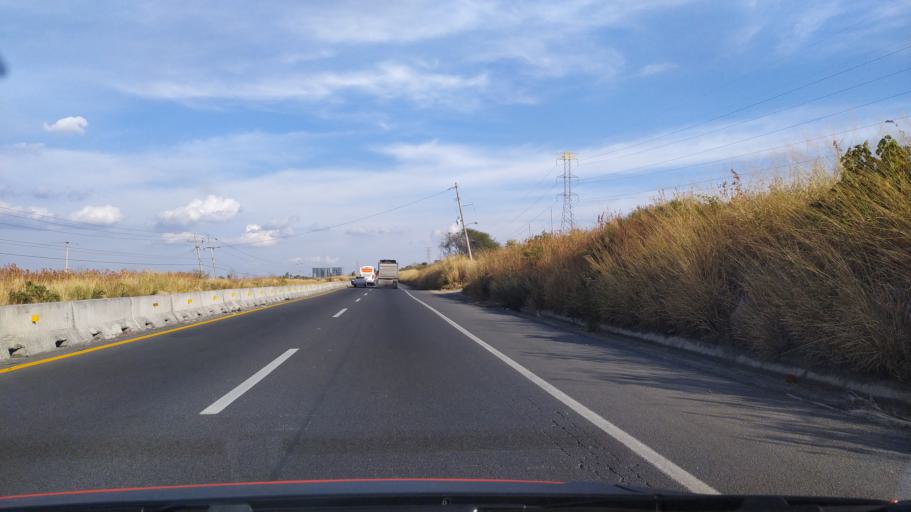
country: MX
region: Jalisco
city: Atotonilquillo
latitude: 20.3956
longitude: -103.0514
